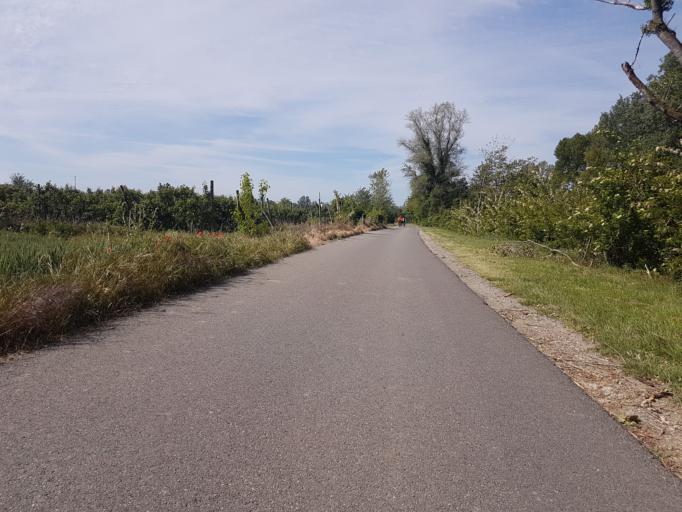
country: FR
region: Rhone-Alpes
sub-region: Departement de l'Ardeche
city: La Voulte-sur-Rhone
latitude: 44.7922
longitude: 4.7805
